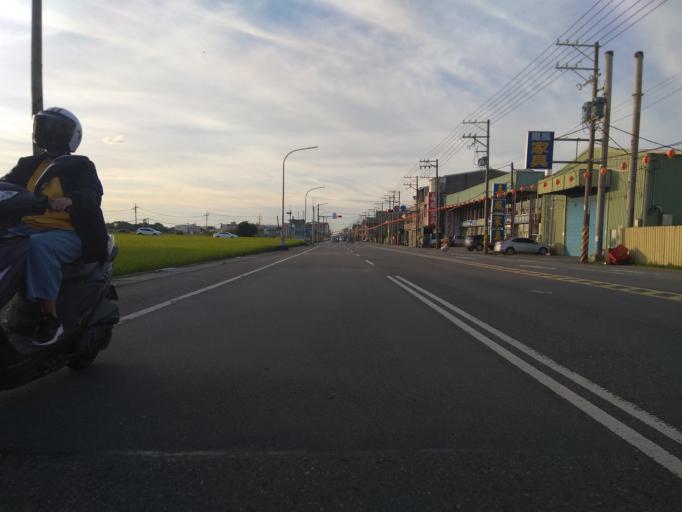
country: TW
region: Taiwan
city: Taoyuan City
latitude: 25.0020
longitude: 121.1541
